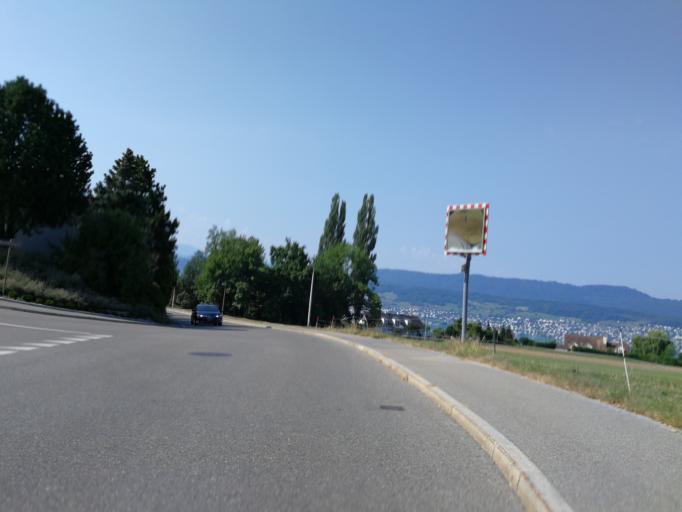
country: CH
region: Zurich
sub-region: Bezirk Meilen
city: Herrliberg
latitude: 47.2978
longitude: 8.6126
